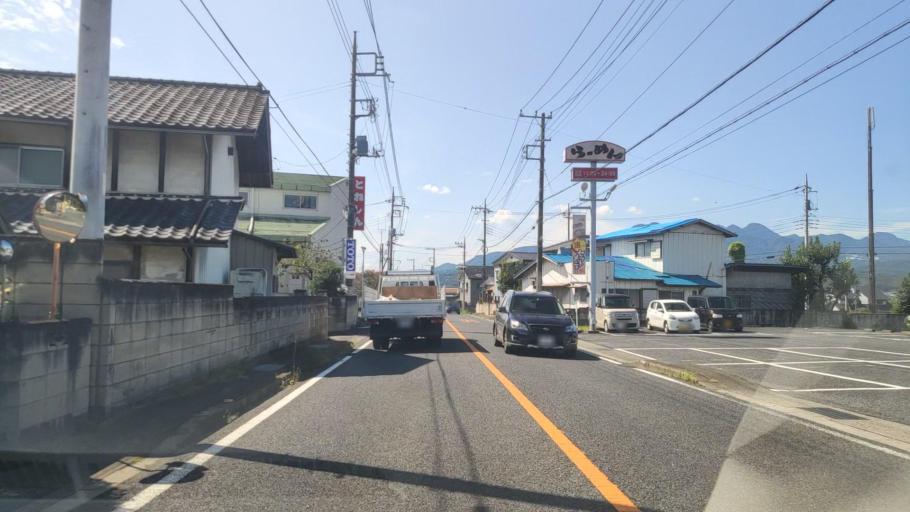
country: JP
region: Gunma
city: Shibukawa
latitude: 36.5267
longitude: 139.0122
